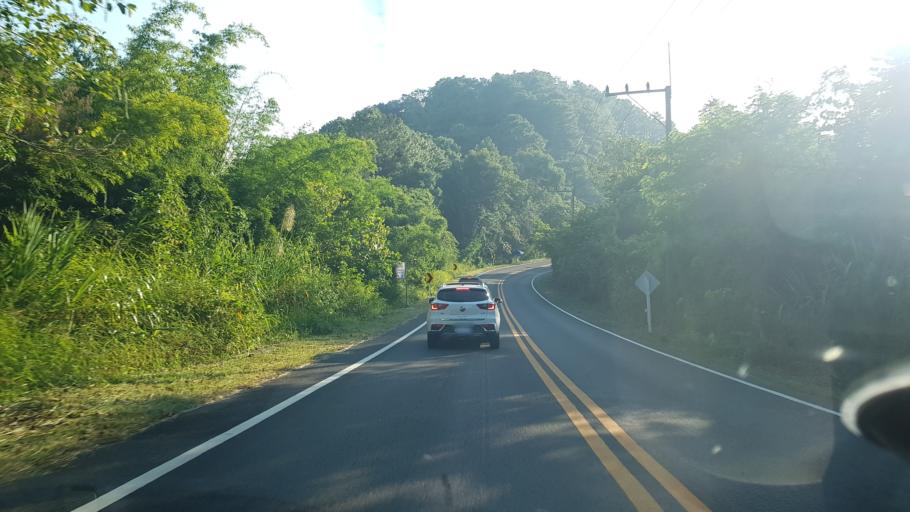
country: TH
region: Chiang Rai
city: Mae Fa Luang
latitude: 20.3092
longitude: 99.8190
